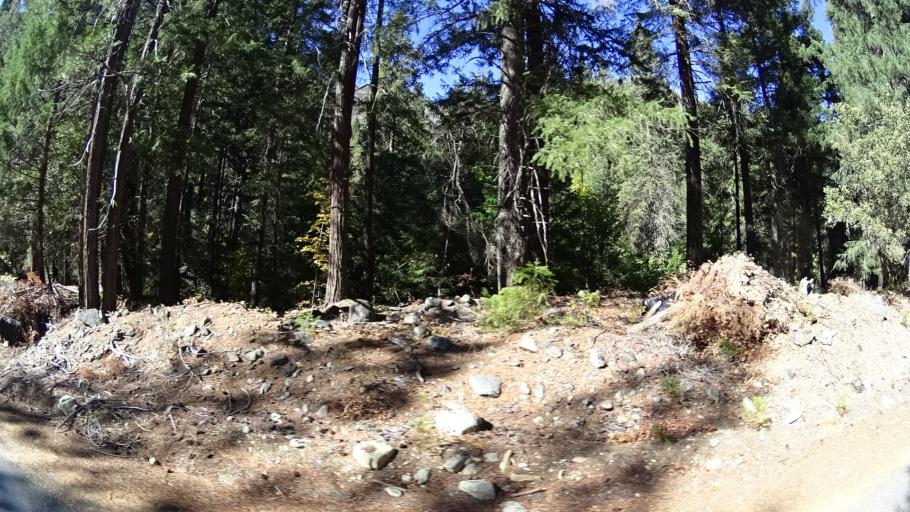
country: US
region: California
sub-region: Siskiyou County
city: Yreka
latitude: 41.3694
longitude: -123.0258
